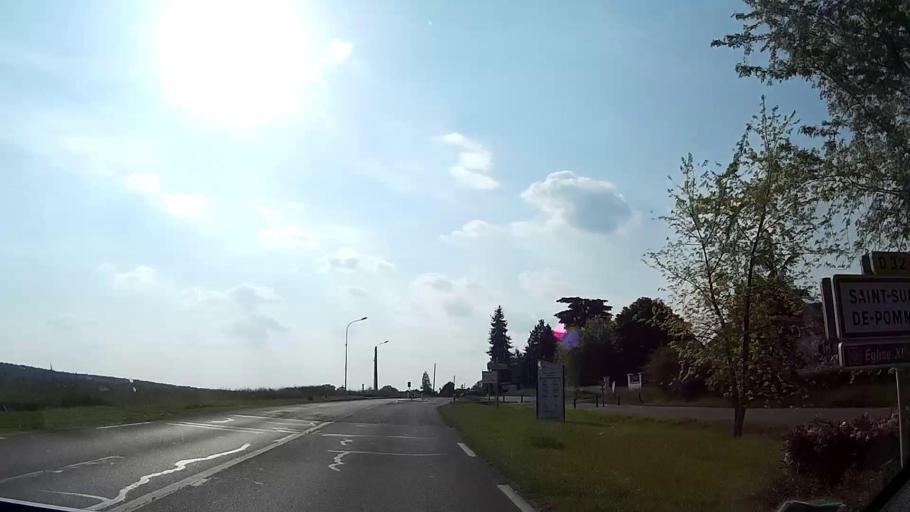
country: FR
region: Centre
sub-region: Departement du Loir-et-Cher
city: Saint-Sulpice-de-Pommeray
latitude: 47.6063
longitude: 1.2779
